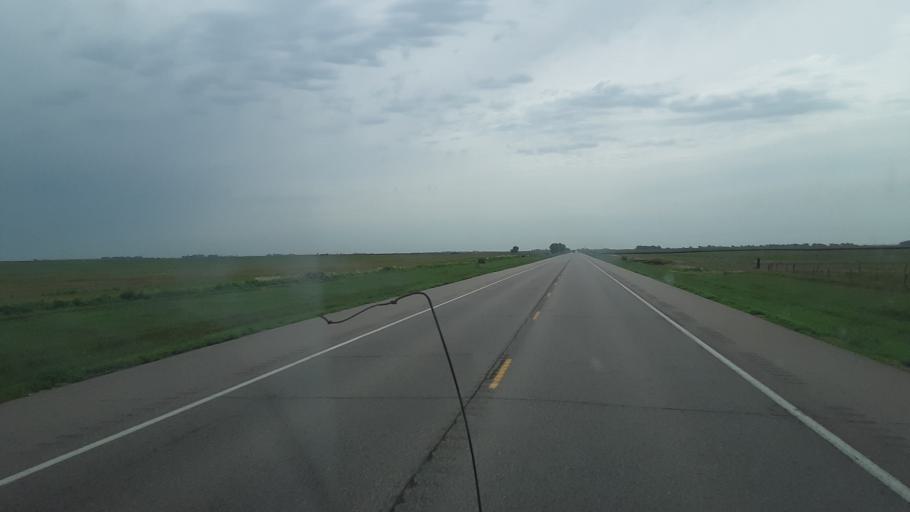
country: US
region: Kansas
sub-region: Stafford County
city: Saint John
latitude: 37.9562
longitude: -98.8937
